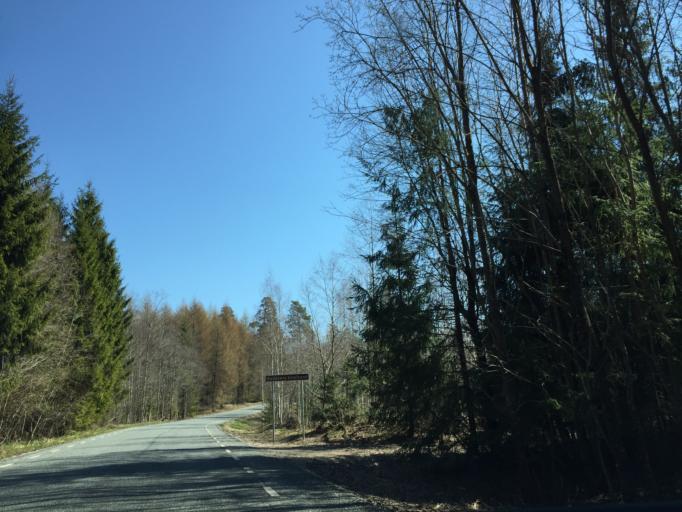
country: EE
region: Tartu
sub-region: Alatskivi vald
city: Kallaste
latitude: 58.5784
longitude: 27.0160
